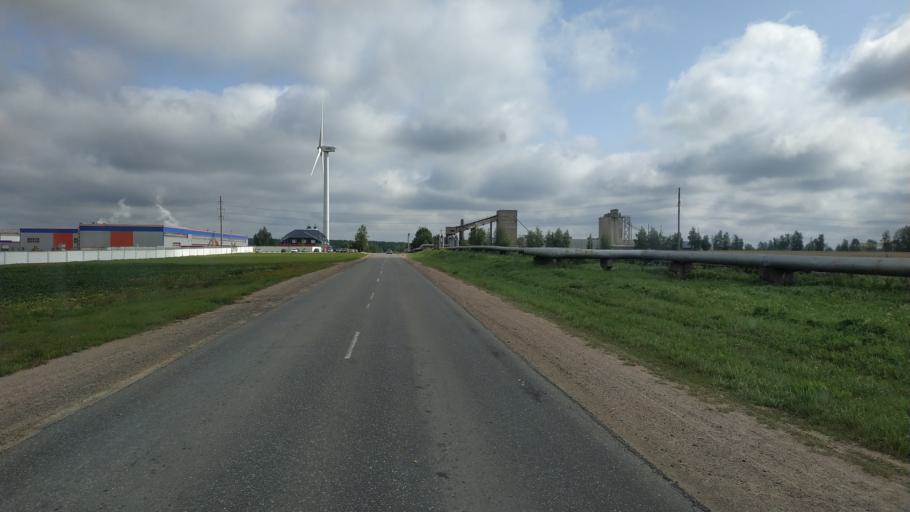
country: BY
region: Mogilev
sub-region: Mahilyowski Rayon
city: Veyno
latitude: 53.8388
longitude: 30.3745
